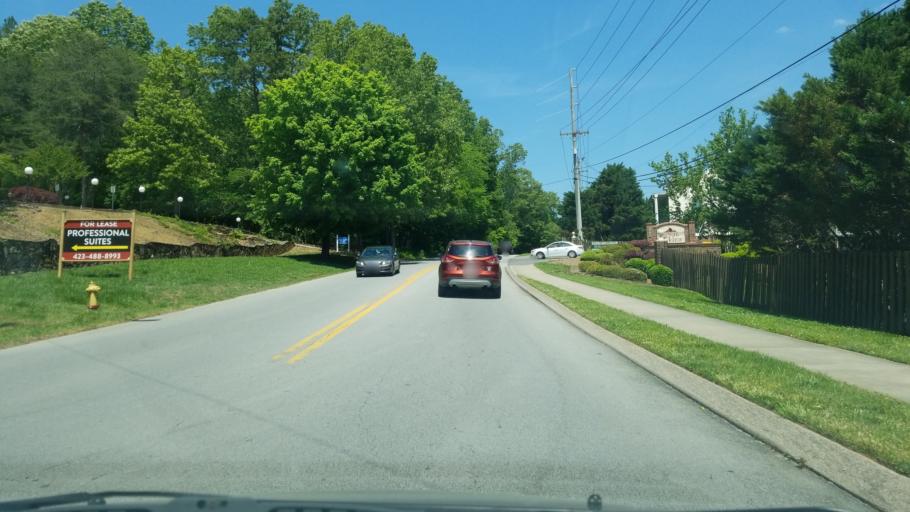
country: US
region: Tennessee
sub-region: Hamilton County
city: Signal Mountain
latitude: 35.1029
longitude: -85.3275
